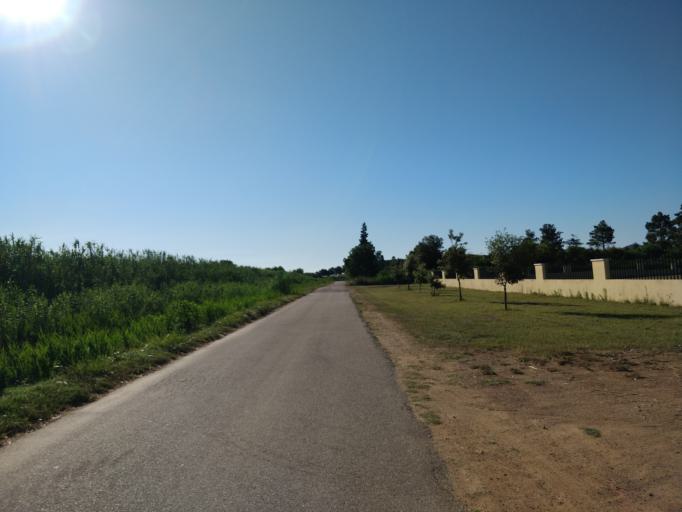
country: IT
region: Sardinia
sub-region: Provincia di Ogliastra
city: Lotzorai
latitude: 39.9606
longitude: 9.6790
